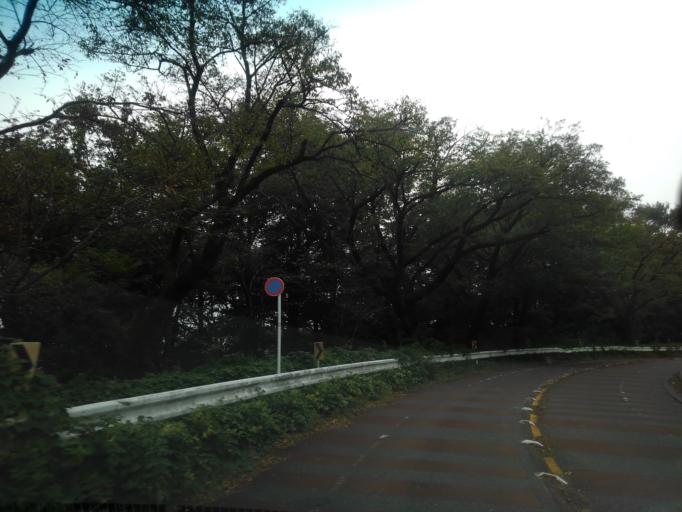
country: JP
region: Tokyo
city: Higashimurayama-shi
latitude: 35.7682
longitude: 139.4380
